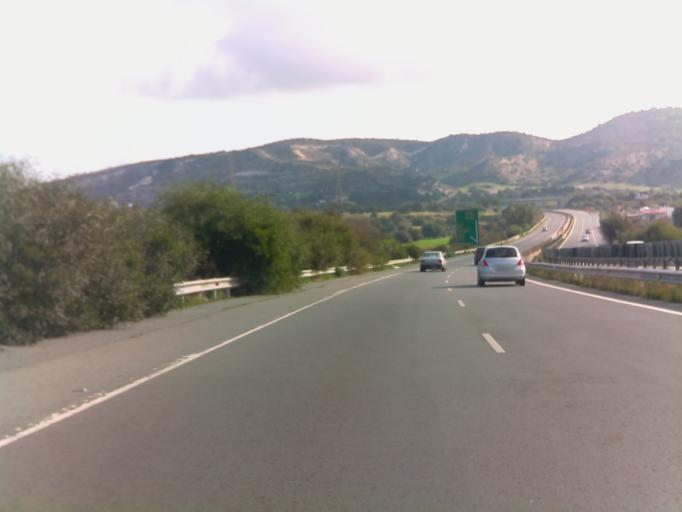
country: CY
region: Limassol
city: Pyrgos
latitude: 34.7219
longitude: 33.1946
